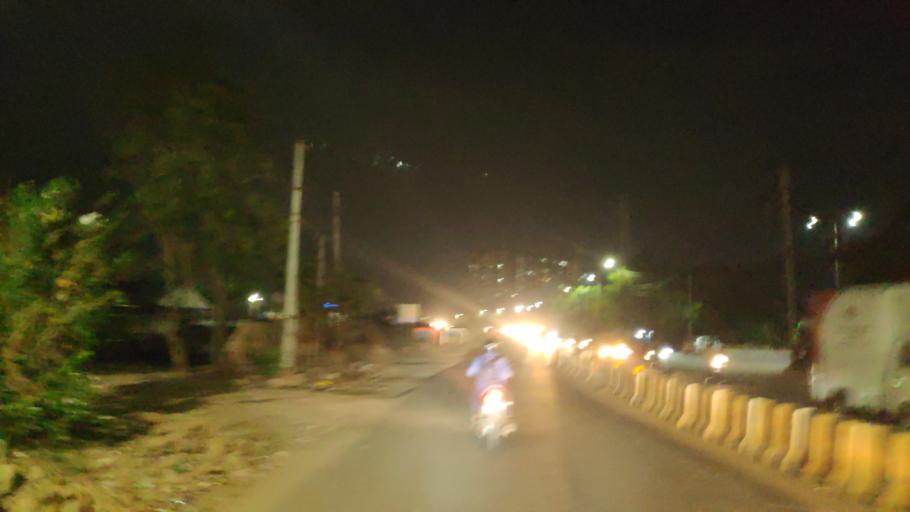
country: IN
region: Telangana
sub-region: Rangareddi
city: Kukatpalli
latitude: 17.4728
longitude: 78.3849
